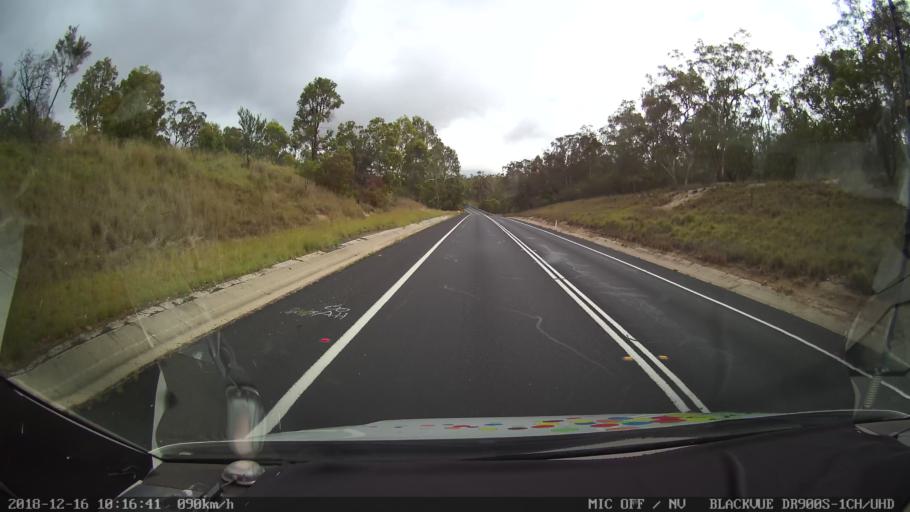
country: AU
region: New South Wales
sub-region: Tenterfield Municipality
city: Carrolls Creek
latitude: -29.2643
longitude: 151.9853
